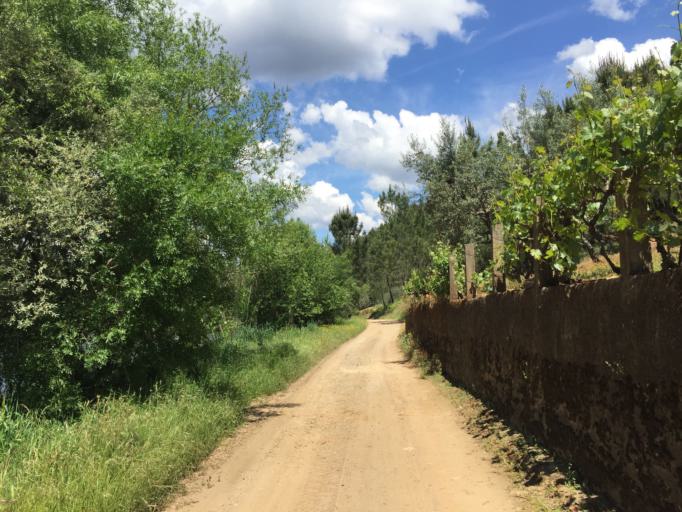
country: PT
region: Coimbra
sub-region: Pampilhosa da Serra
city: Pampilhosa da Serra
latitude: 40.0756
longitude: -7.7860
